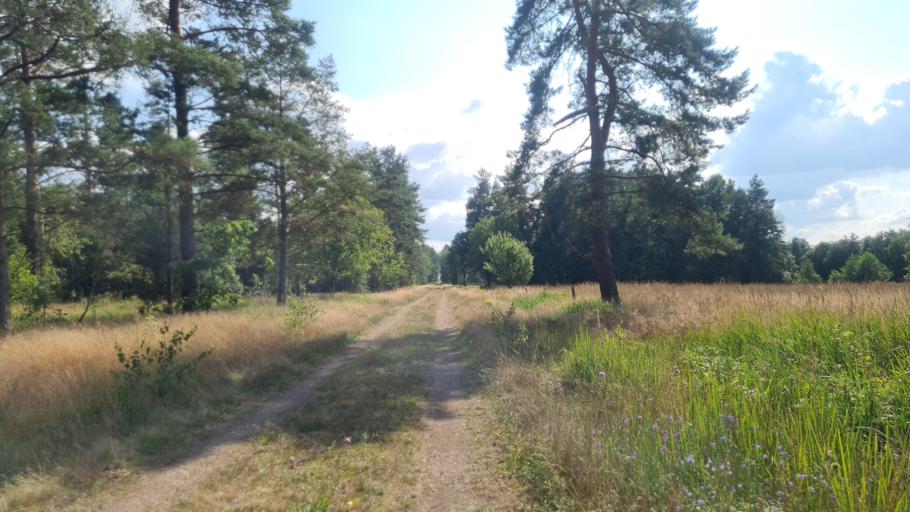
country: SE
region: Kronoberg
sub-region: Ljungby Kommun
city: Ljungby
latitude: 56.7673
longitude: 13.8950
